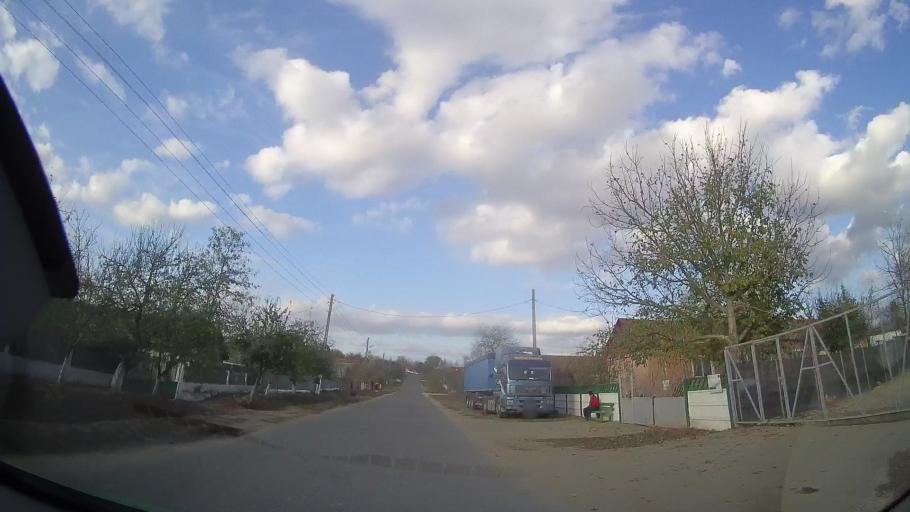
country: RO
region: Constanta
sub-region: Comuna Cerchezu
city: Cerchezu
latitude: 43.8579
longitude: 28.1013
